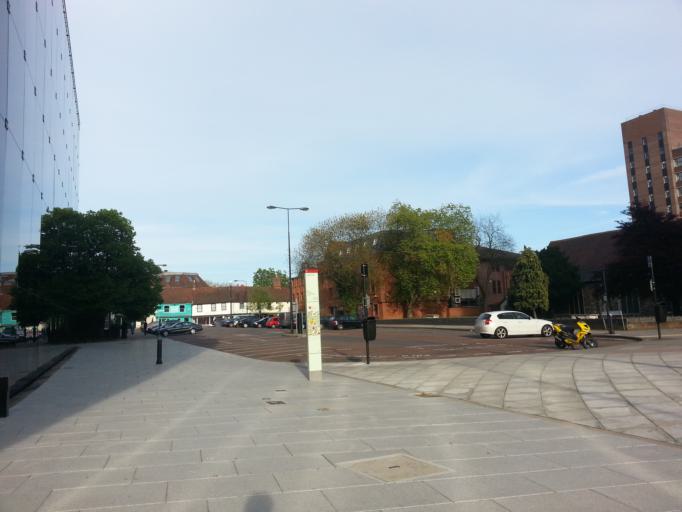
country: GB
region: England
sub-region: Suffolk
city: Ipswich
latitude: 52.0552
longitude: 1.1508
